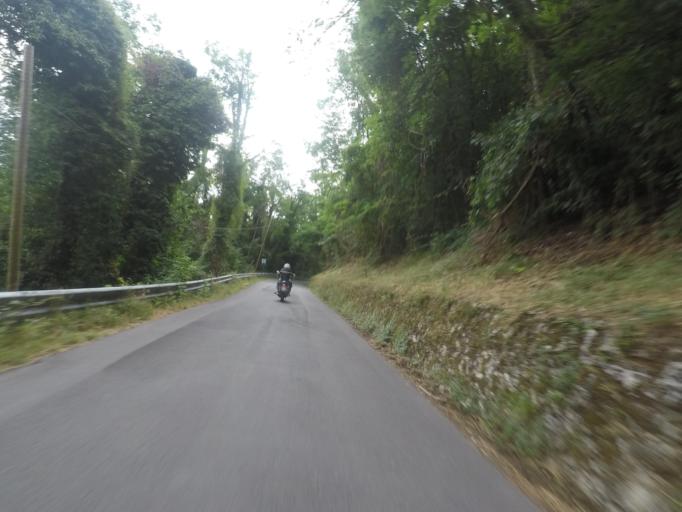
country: IT
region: Tuscany
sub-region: Provincia di Lucca
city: Castelnuovo di Garfagnana
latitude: 44.1082
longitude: 10.3728
